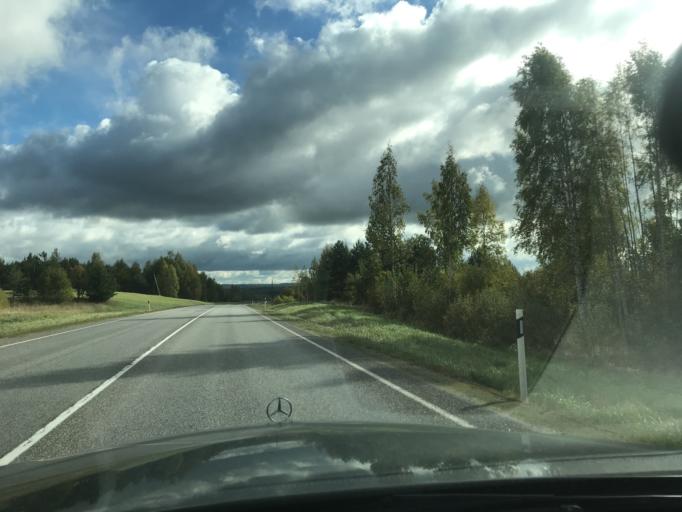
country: EE
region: Vorumaa
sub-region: Voru linn
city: Voru
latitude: 57.7477
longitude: 27.2447
